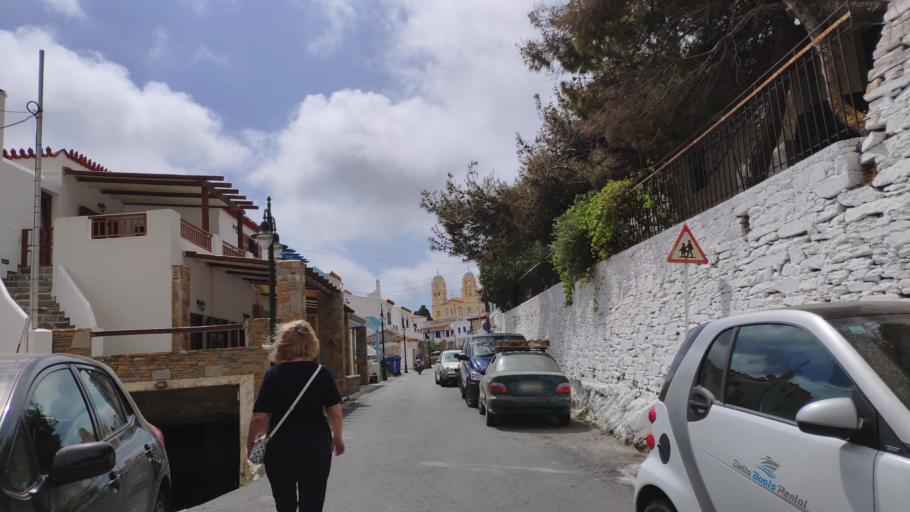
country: GR
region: South Aegean
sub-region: Nomos Kykladon
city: Kythnos
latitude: 37.3844
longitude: 24.4293
